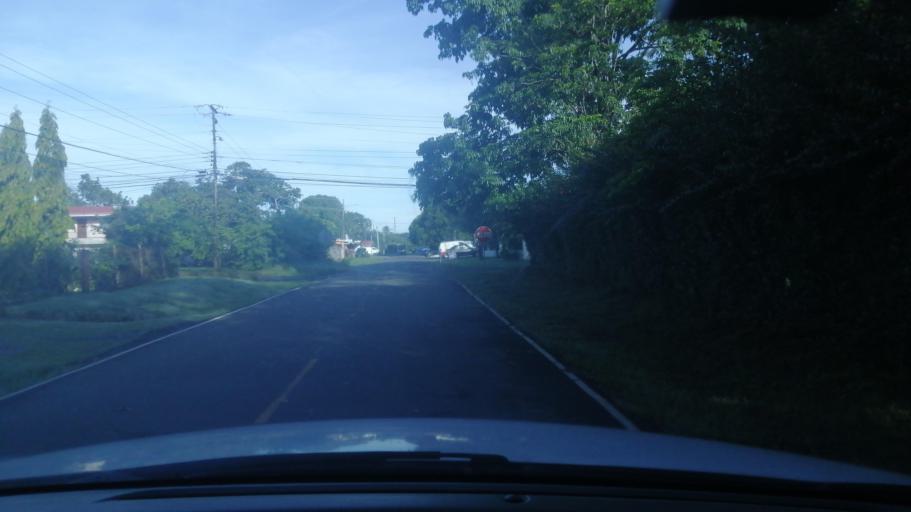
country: PA
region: Chiriqui
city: David
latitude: 8.4484
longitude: -82.4230
